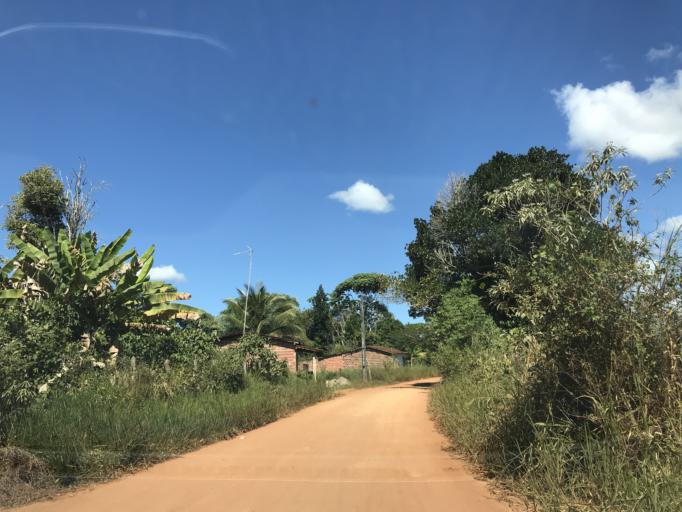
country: BR
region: Bahia
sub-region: Valenca
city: Valenca
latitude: -13.3179
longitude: -39.2401
